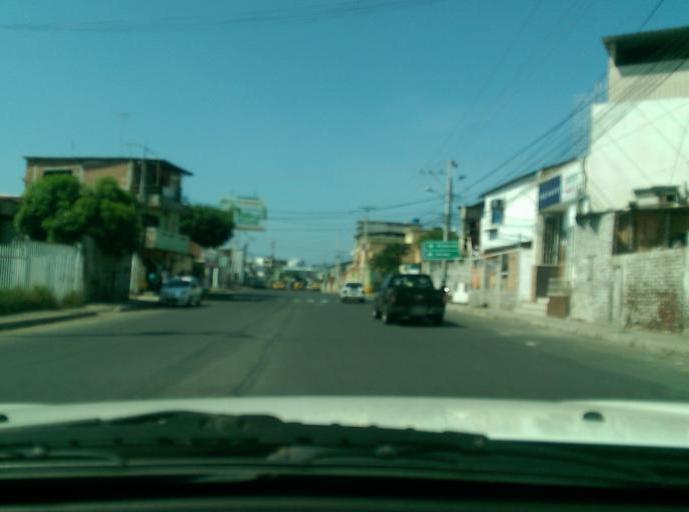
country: EC
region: Manabi
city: Manta
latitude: -0.9483
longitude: -80.7398
